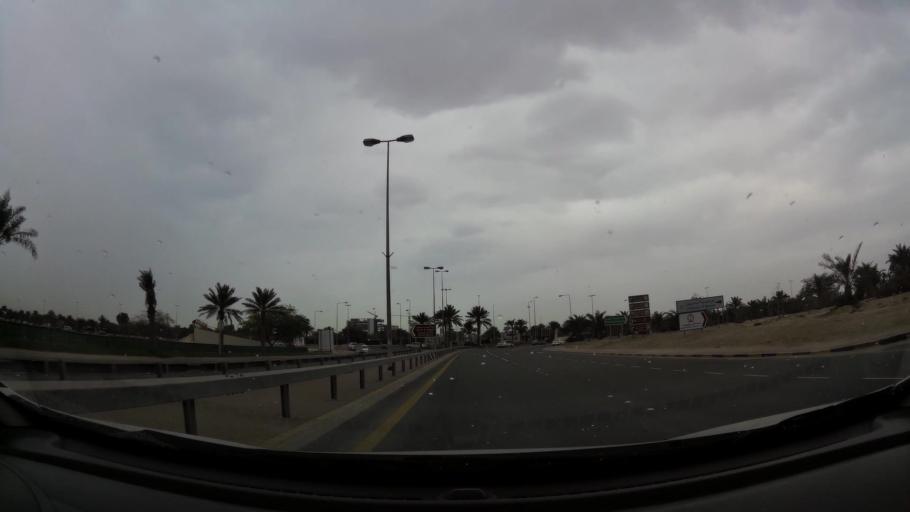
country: BH
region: Northern
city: Ar Rifa'
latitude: 26.0984
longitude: 50.5445
